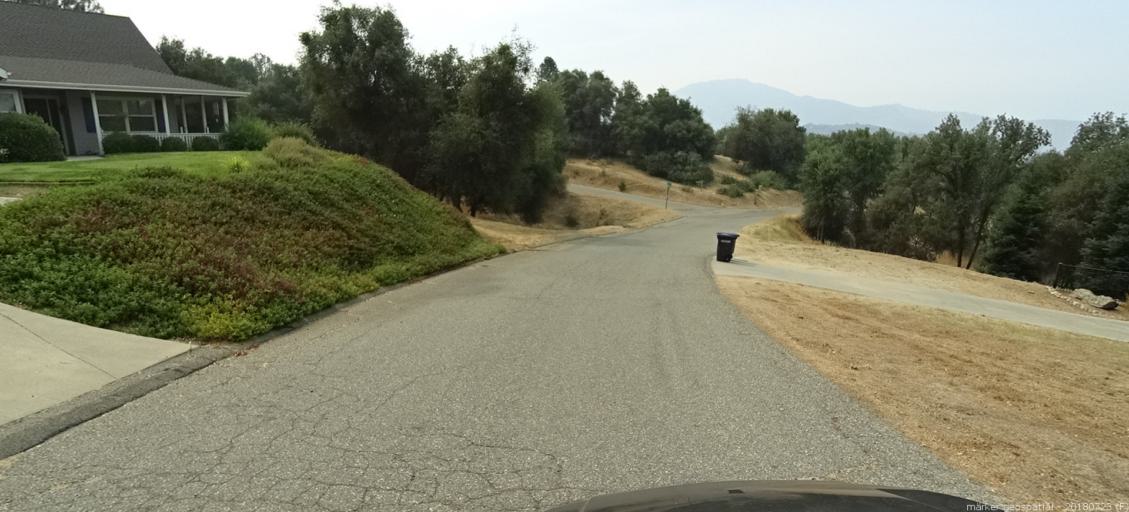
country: US
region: California
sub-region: Madera County
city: Ahwahnee
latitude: 37.3689
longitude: -119.6983
